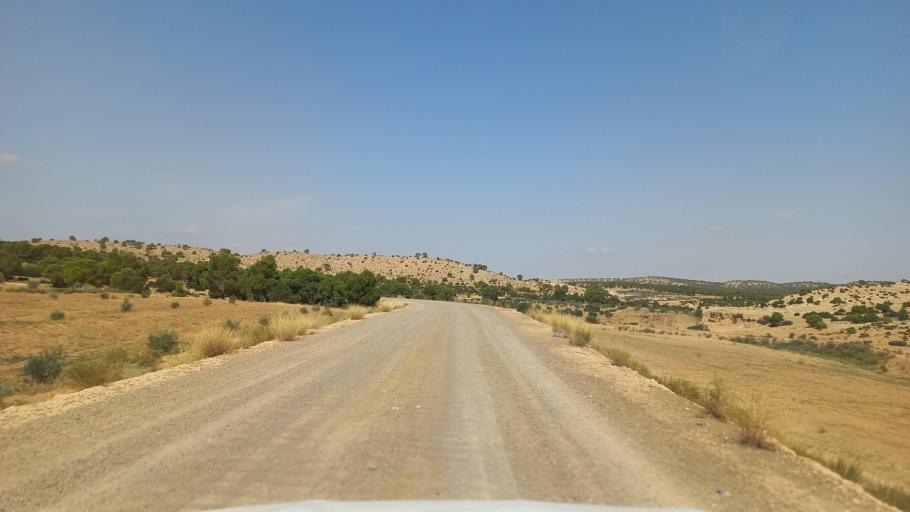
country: TN
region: Al Qasrayn
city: Sbiba
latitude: 35.3917
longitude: 8.9514
